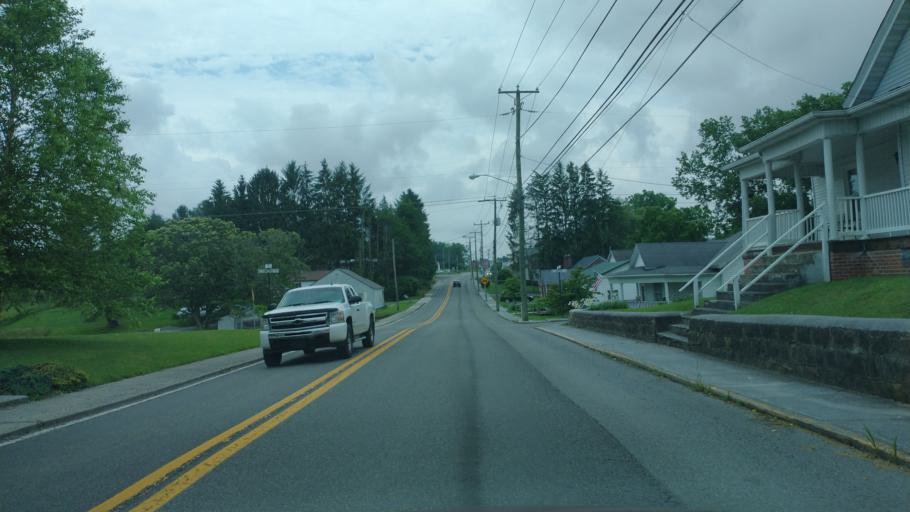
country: US
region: West Virginia
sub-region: Mercer County
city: Athens
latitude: 37.4191
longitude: -81.0156
